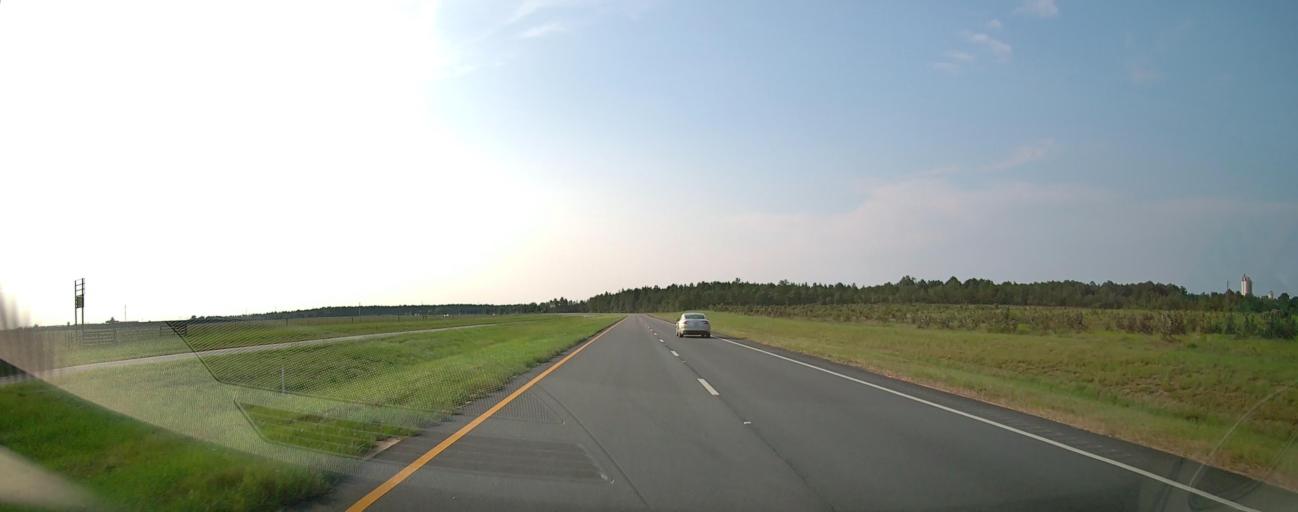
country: US
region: Georgia
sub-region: Taylor County
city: Butler
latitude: 32.5604
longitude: -84.2668
